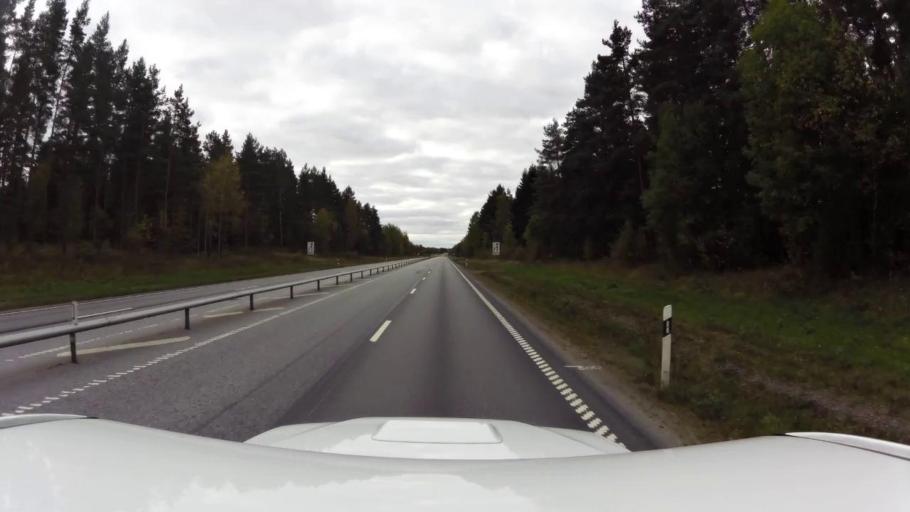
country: SE
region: OEstergoetland
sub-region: Linkopings Kommun
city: Malmslatt
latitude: 58.3761
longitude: 15.5429
